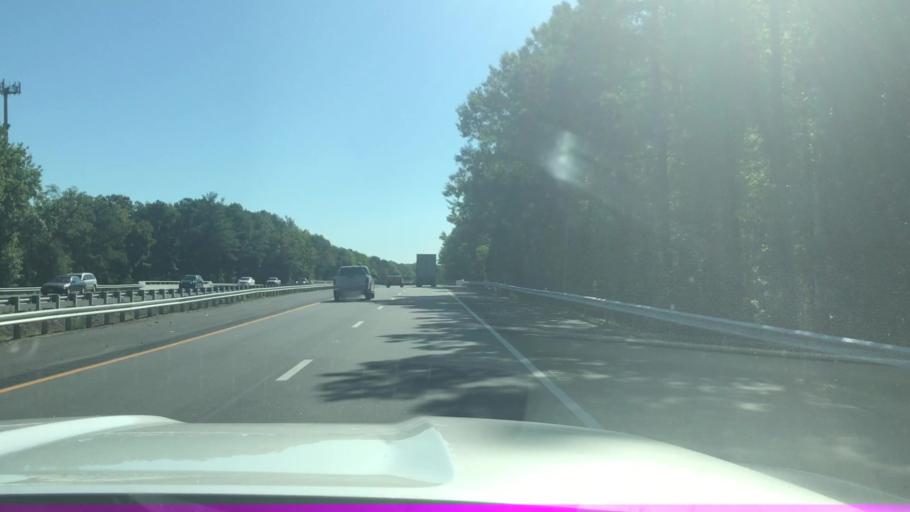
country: US
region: Virginia
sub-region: Henrico County
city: Sandston
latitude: 37.5293
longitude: -77.3135
